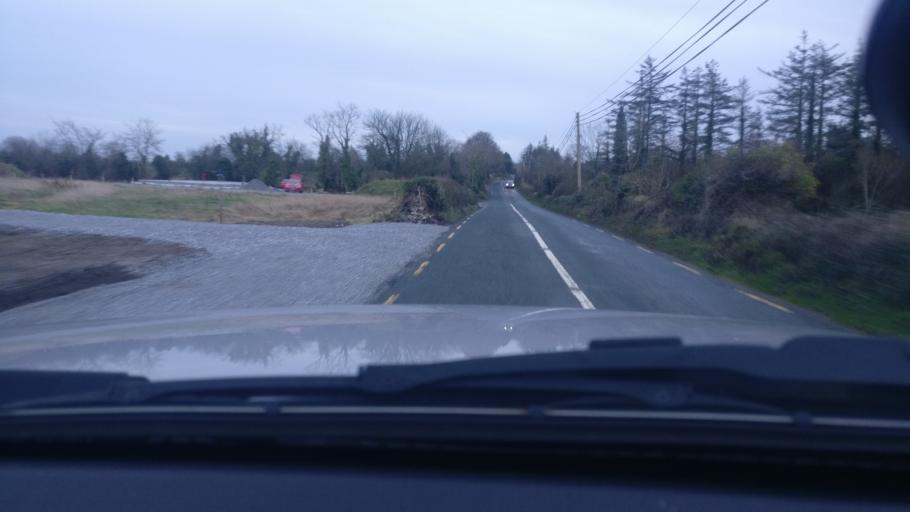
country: IE
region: Connaught
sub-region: County Galway
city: Loughrea
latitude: 53.1705
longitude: -8.5238
